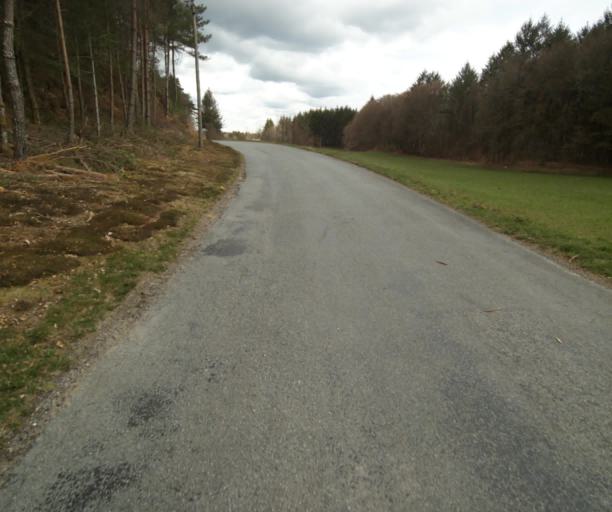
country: FR
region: Limousin
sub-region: Departement de la Correze
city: Correze
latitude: 45.3238
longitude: 1.9545
